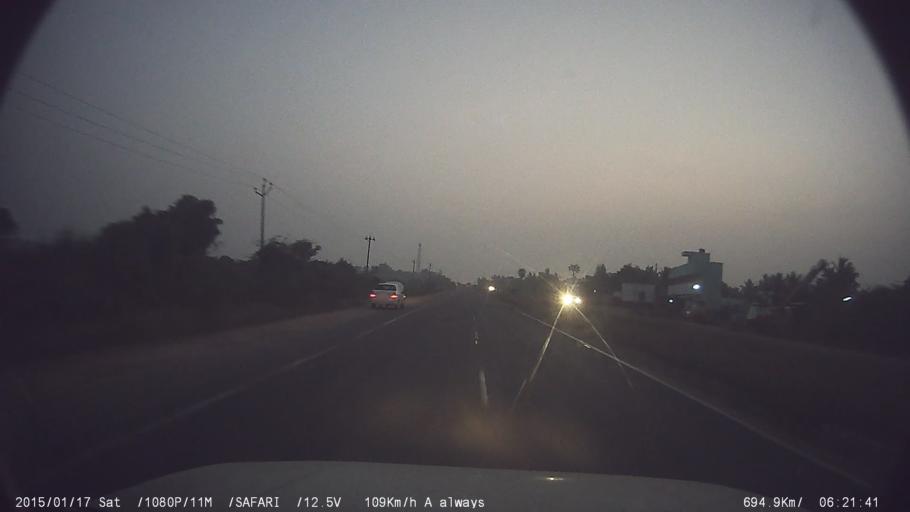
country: IN
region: Tamil Nadu
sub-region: Kancheepuram
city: Wallajahbad
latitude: 12.9065
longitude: 79.8286
